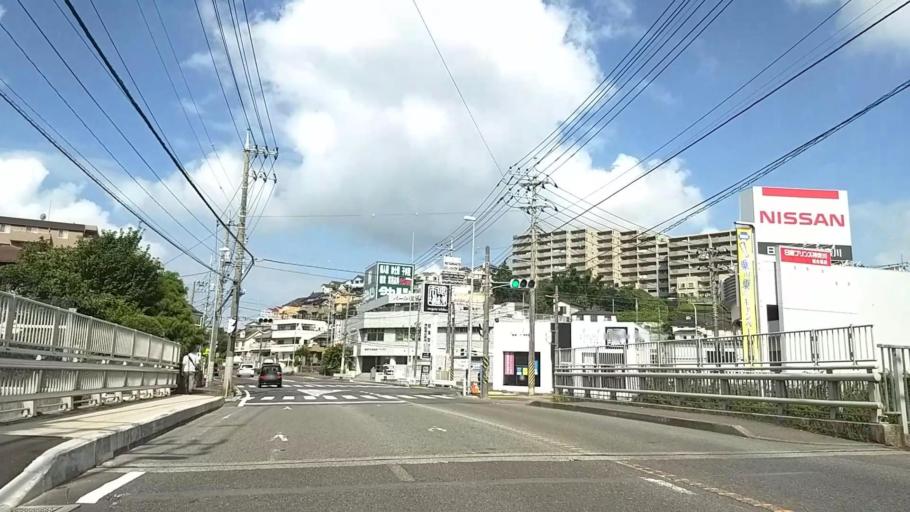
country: JP
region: Kanagawa
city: Yokohama
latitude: 35.4796
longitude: 139.5582
